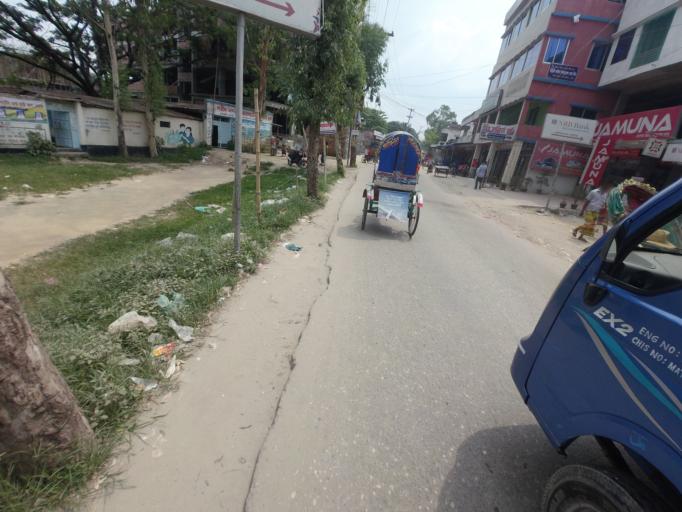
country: BD
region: Dhaka
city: Azimpur
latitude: 23.7324
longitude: 90.3347
